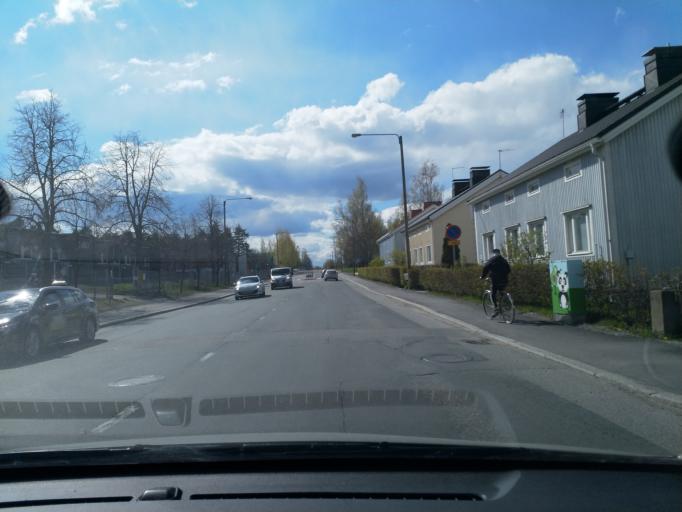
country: FI
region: Pirkanmaa
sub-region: Tampere
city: Tampere
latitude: 61.4826
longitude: 23.7965
